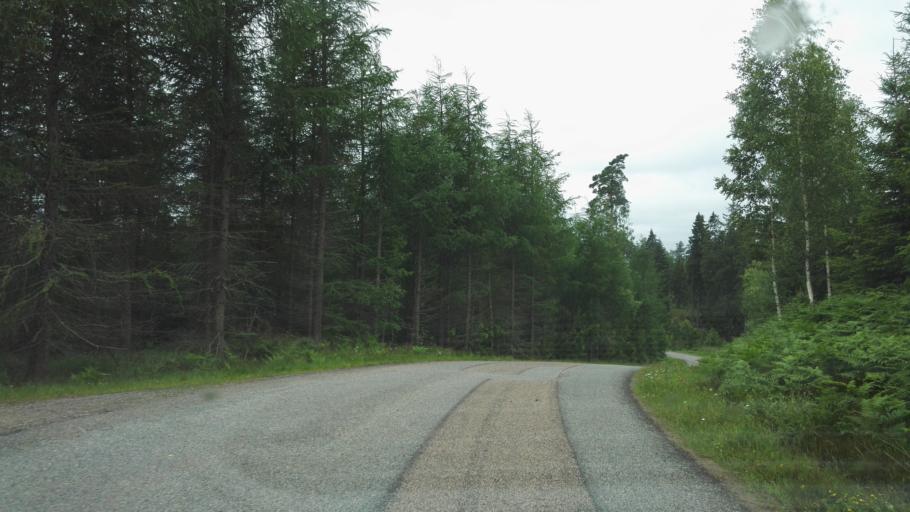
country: SE
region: Joenkoeping
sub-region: Vetlanda Kommun
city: Landsbro
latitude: 57.2111
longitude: 14.8029
